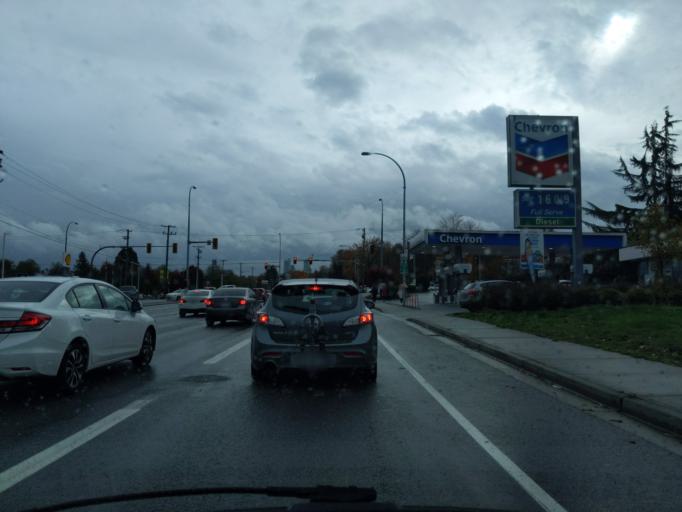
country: CA
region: British Columbia
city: Burnaby
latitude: 49.2555
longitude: -123.0045
